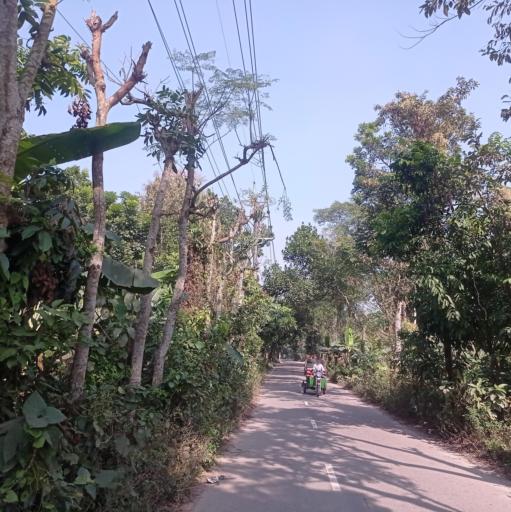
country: BD
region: Dhaka
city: Narsingdi
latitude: 24.0272
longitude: 90.6712
